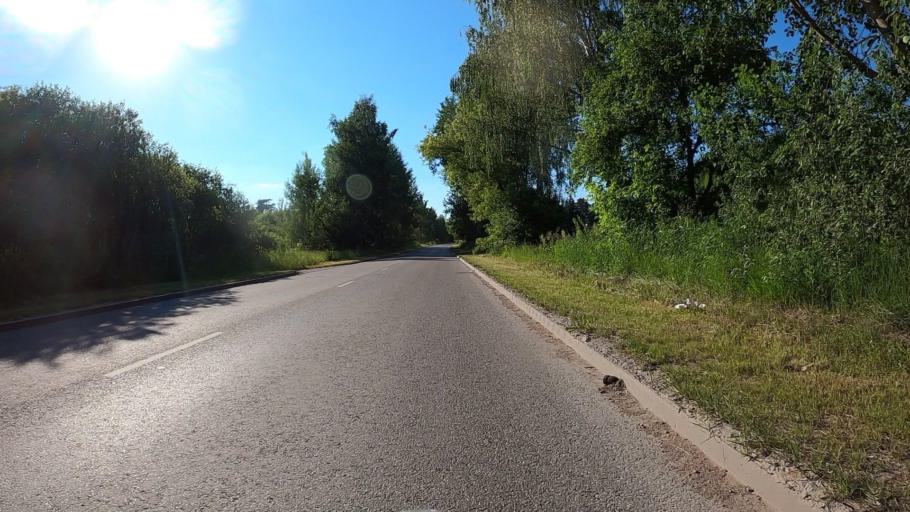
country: LV
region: Kekava
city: Kekava
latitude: 56.8859
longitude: 24.2524
